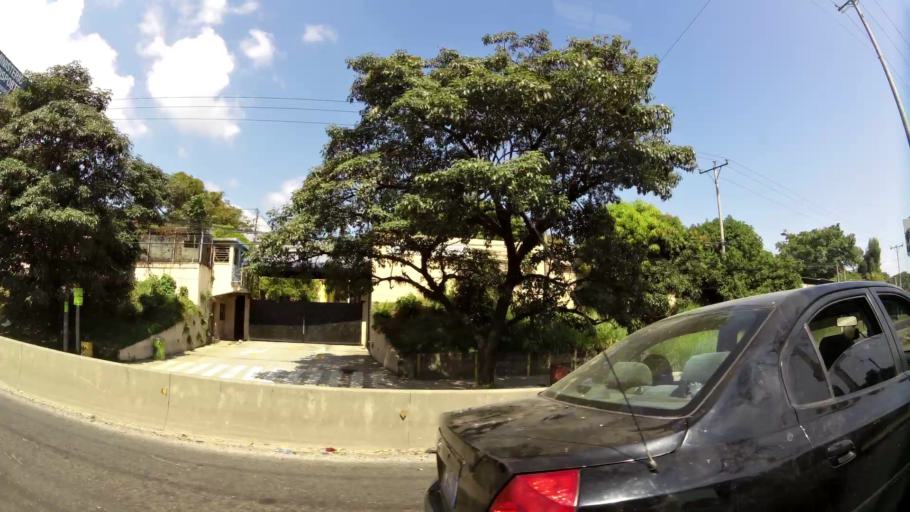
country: SV
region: La Libertad
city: Antiguo Cuscatlan
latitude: 13.6688
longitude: -89.2662
